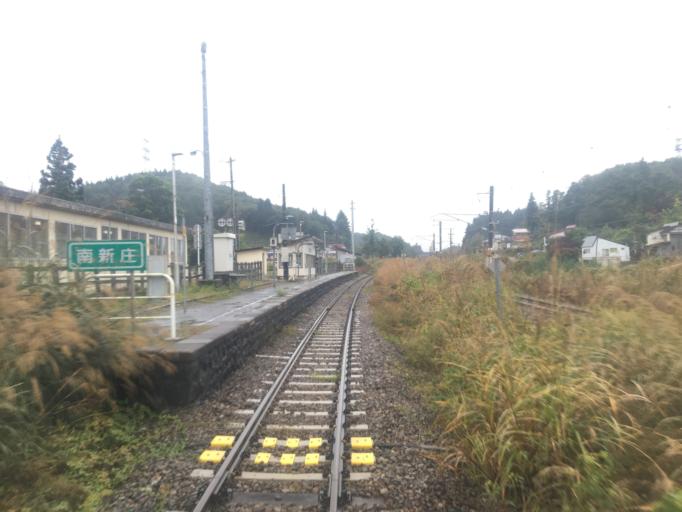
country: JP
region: Yamagata
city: Shinjo
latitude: 38.7216
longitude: 140.3163
